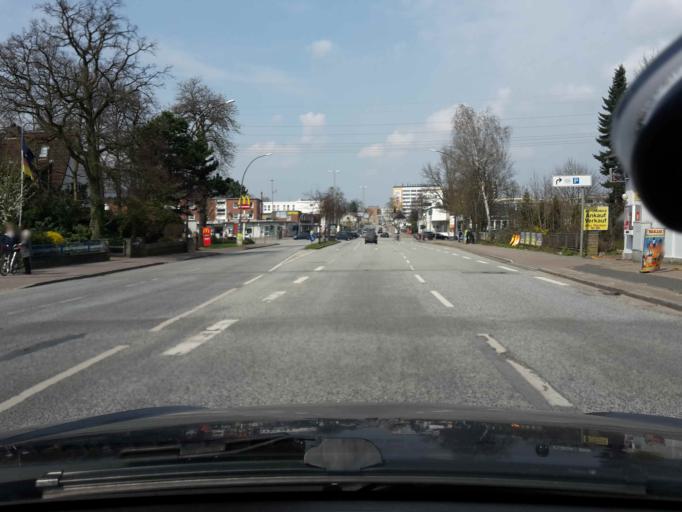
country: DE
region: Hamburg
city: Eidelstedt
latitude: 53.5875
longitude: 9.8771
